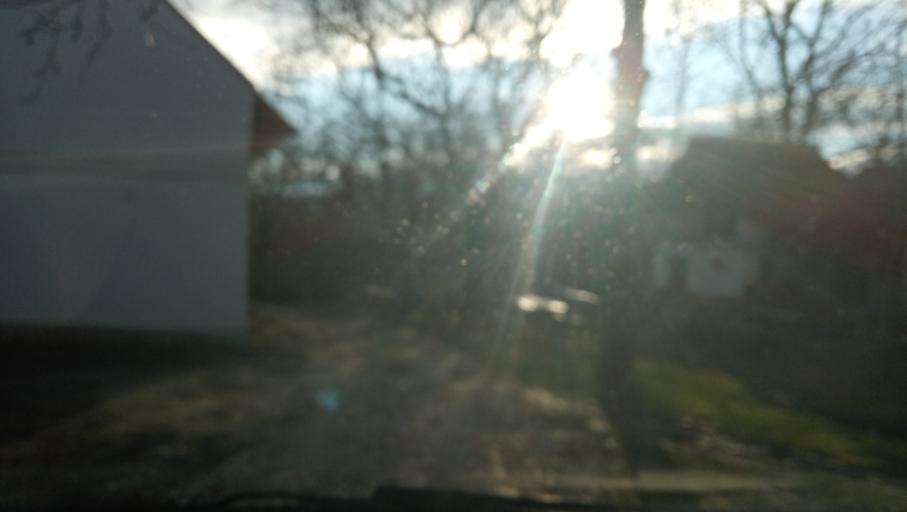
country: HU
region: Komarom-Esztergom
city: Piliscsev
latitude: 47.6845
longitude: 18.8297
